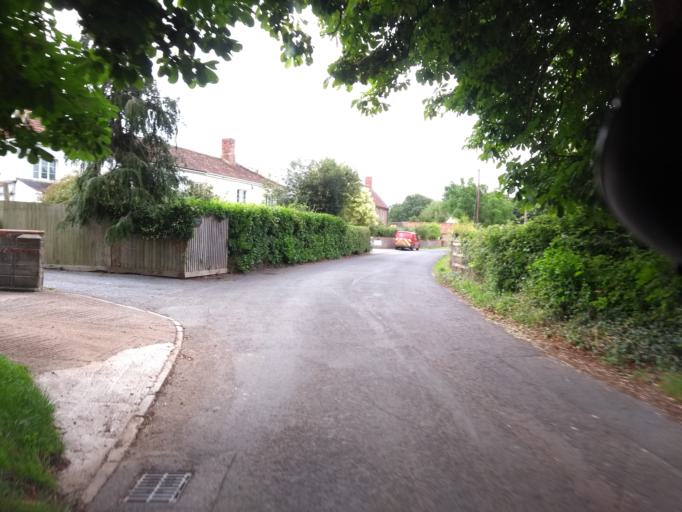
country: GB
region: England
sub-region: Somerset
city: Bridgwater
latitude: 51.1060
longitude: -2.9831
